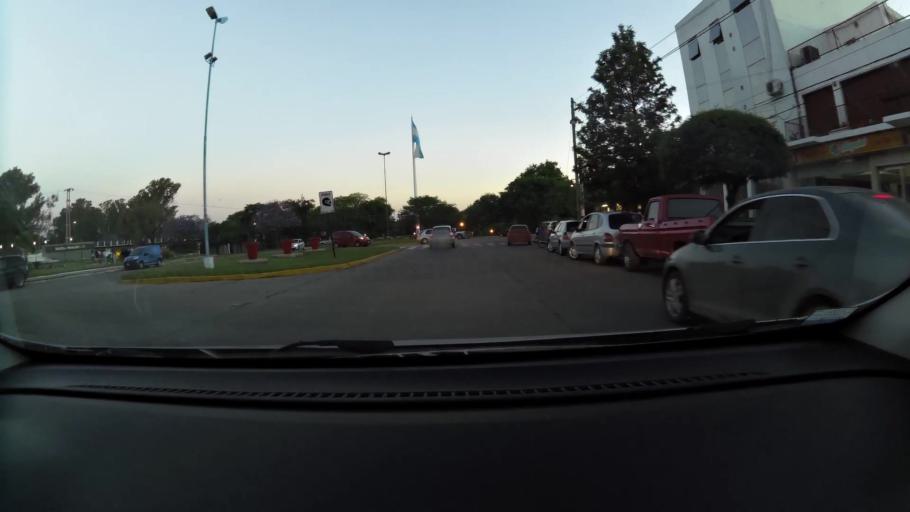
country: AR
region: Cordoba
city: Villa Nueva
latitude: -32.4211
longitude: -63.2462
